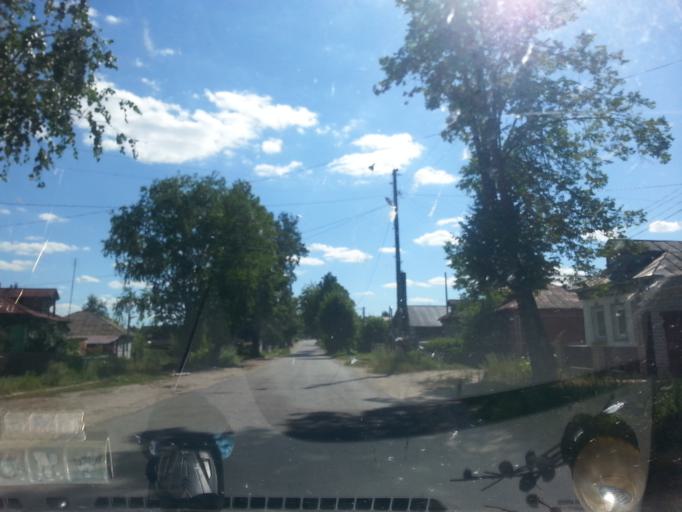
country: RU
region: Nizjnij Novgorod
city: Taremskoye
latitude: 55.9922
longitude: 43.0123
